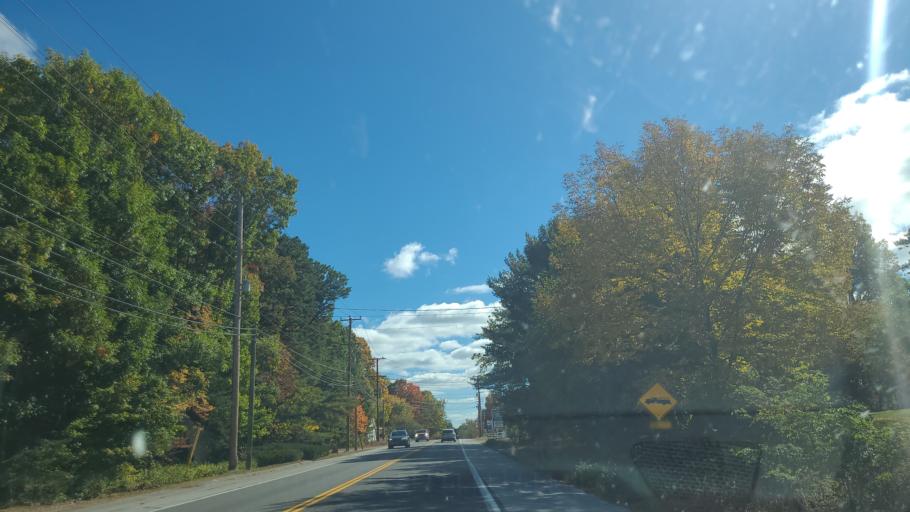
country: US
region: Maine
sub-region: Cumberland County
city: Bridgton
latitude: 43.9740
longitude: -70.6152
